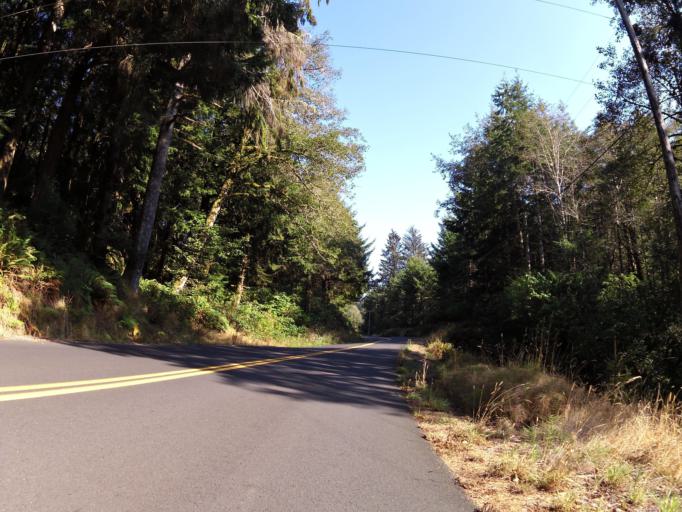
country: US
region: Oregon
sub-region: Lincoln County
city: Rose Lodge
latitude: 45.0853
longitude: -123.9547
